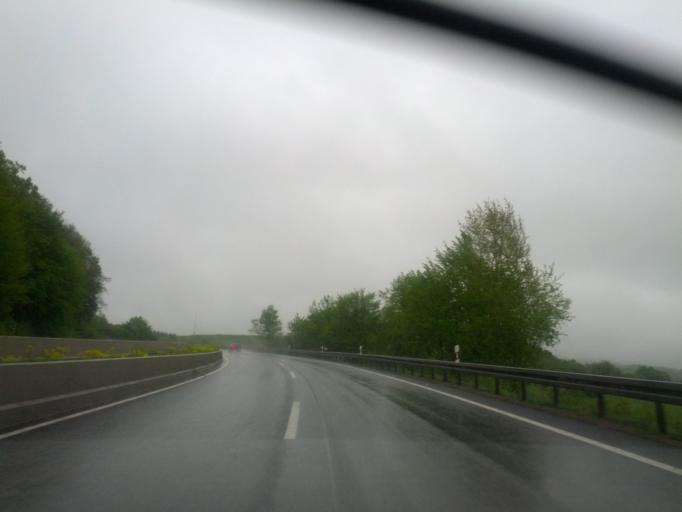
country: DE
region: Hesse
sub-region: Regierungsbezirk Giessen
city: Reiskirchen
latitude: 50.6094
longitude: 8.8280
